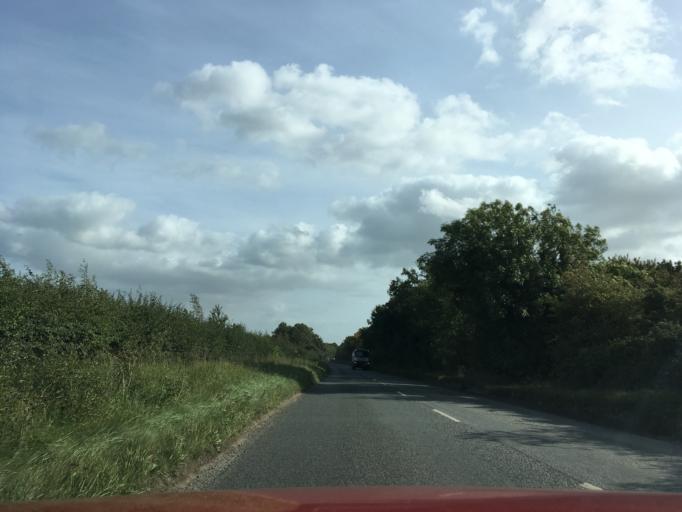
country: GB
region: England
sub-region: South Gloucestershire
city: Charfield
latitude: 51.6109
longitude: -2.4117
